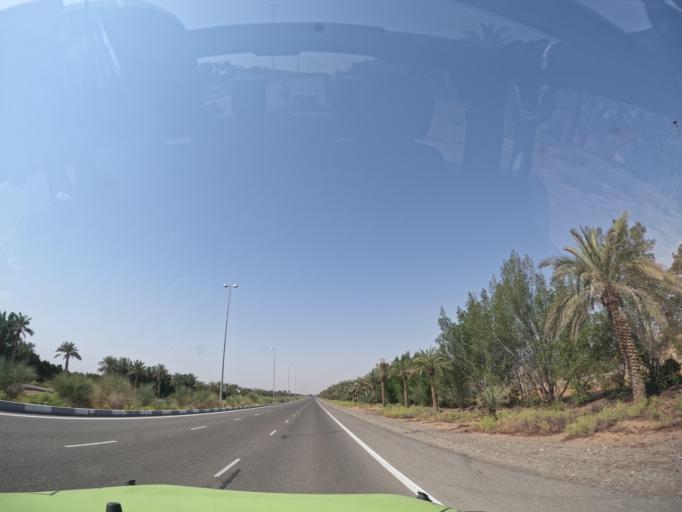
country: AE
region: Abu Dhabi
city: Al Ain
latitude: 24.2124
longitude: 55.6077
